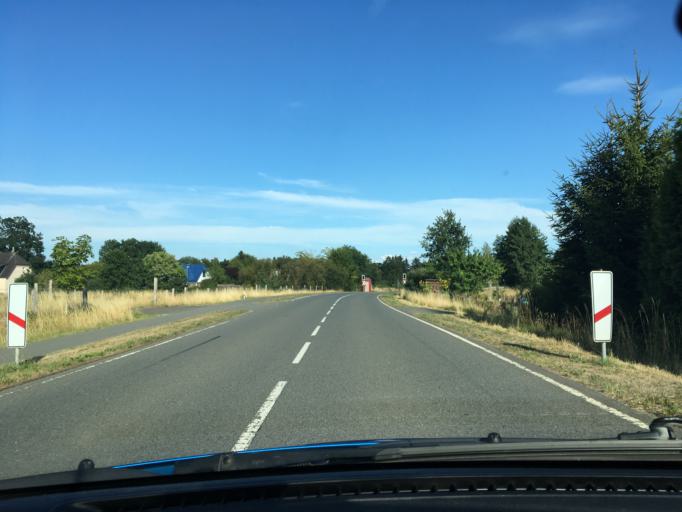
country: DE
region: Lower Saxony
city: Bleckede
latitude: 53.2954
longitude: 10.7195
